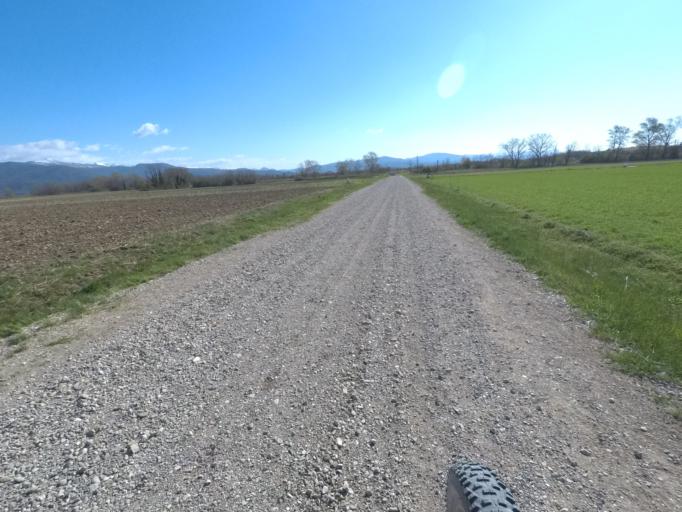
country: IT
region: Friuli Venezia Giulia
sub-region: Provincia di Udine
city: Moimacco
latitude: 46.0907
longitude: 13.3488
